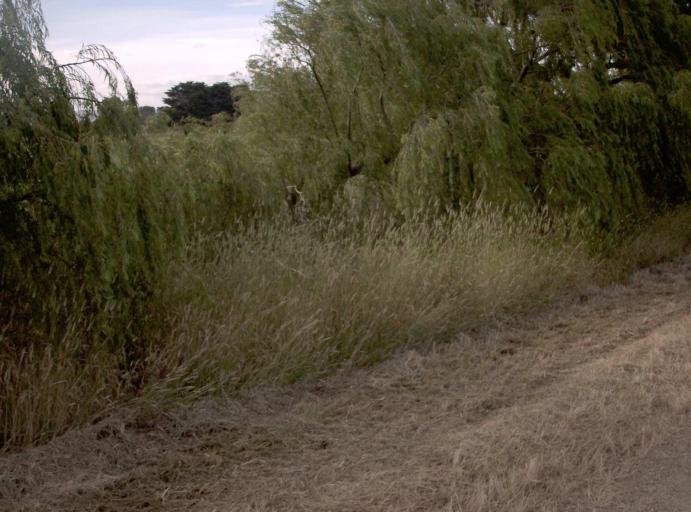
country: AU
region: Victoria
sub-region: Wellington
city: Heyfield
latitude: -38.0069
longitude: 146.7800
